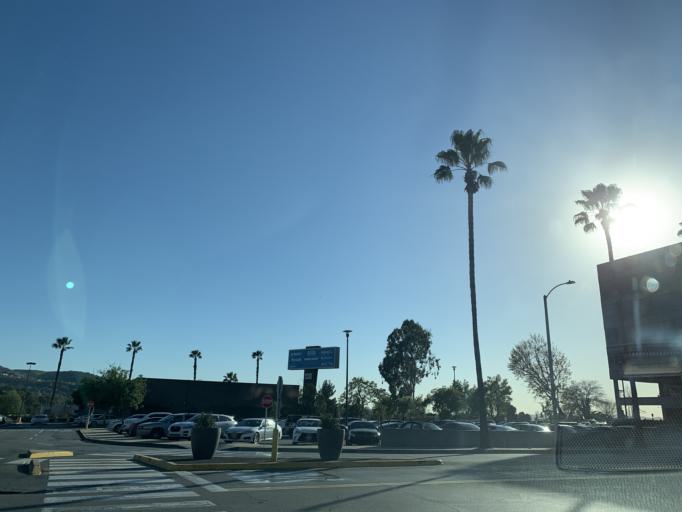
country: US
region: California
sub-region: Los Angeles County
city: Covina
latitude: 34.0737
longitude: -117.8883
